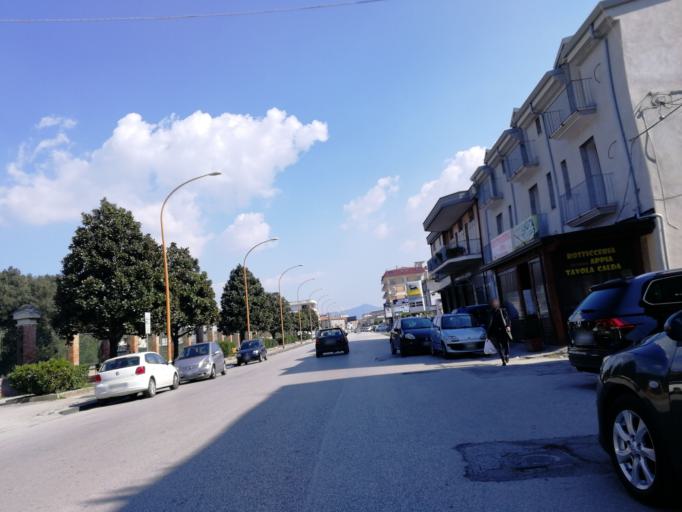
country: IT
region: Campania
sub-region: Provincia di Caserta
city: San Prisco
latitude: 41.0817
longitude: 14.2657
